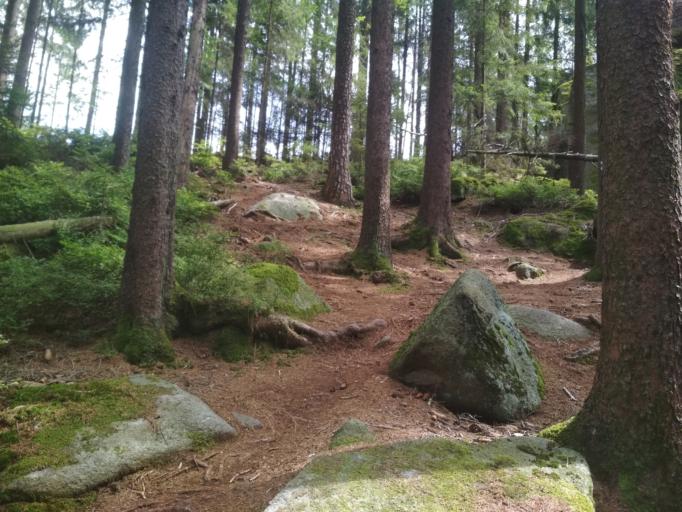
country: CZ
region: Jihocesky
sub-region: Okres Cesky Krumlov
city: Loucovice
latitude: 48.6318
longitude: 14.2619
